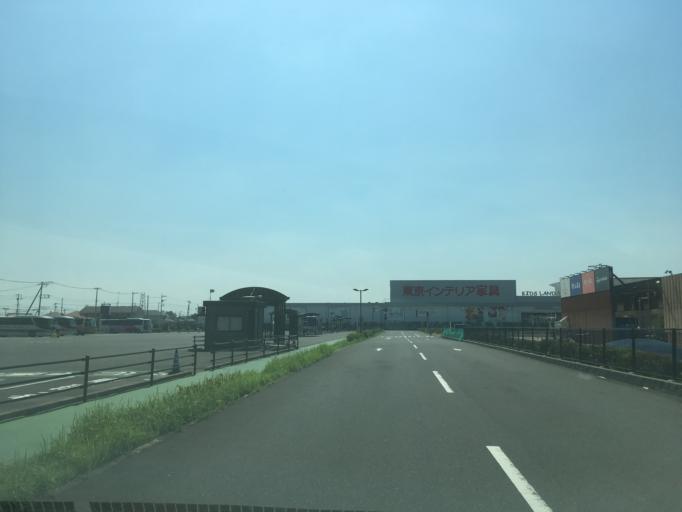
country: JP
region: Chiba
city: Kisarazu
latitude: 35.4348
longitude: 139.9378
